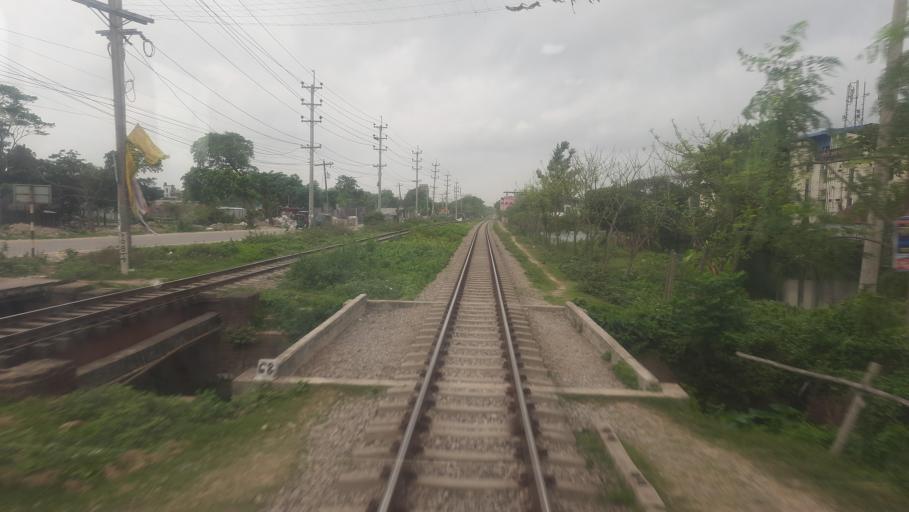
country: BD
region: Dhaka
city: Narsingdi
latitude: 23.9310
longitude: 90.7161
